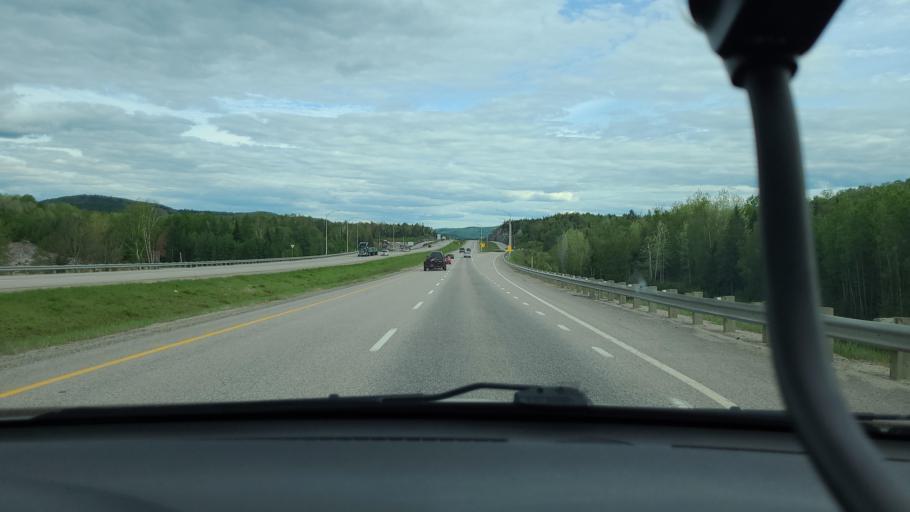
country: CA
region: Quebec
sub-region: Laurentides
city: Labelle
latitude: 46.2622
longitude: -74.7285
